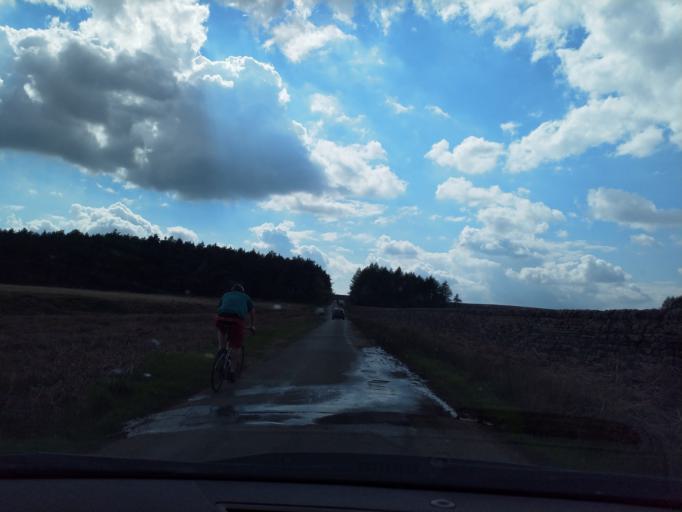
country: GB
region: England
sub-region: Derbyshire
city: Hathersage
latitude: 53.3556
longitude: -1.6546
